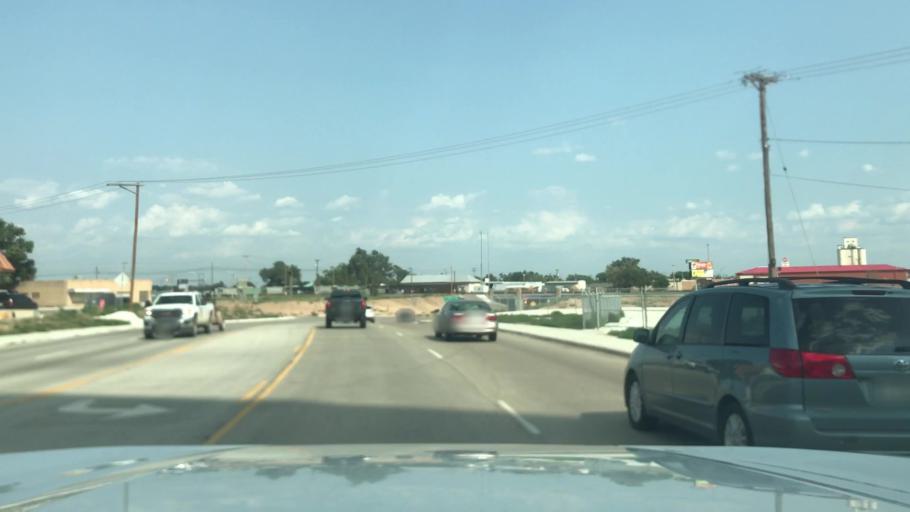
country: US
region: Texas
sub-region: Dallam County
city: Dalhart
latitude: 36.0673
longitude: -102.5243
